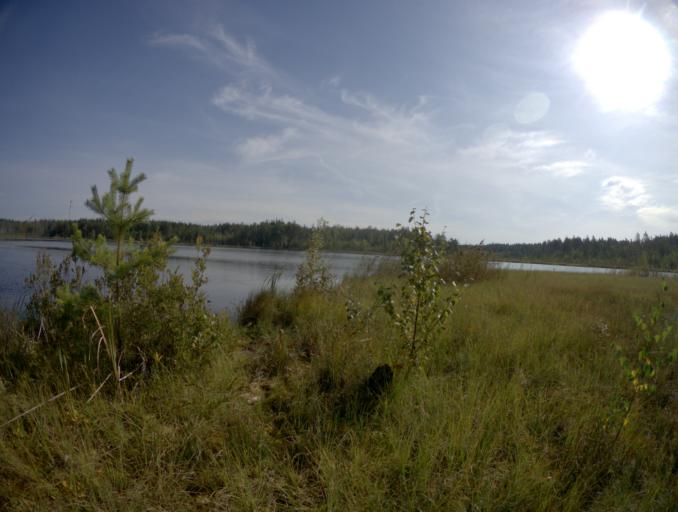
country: RU
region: Moskovskaya
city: Vereya
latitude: 55.8338
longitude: 39.1027
